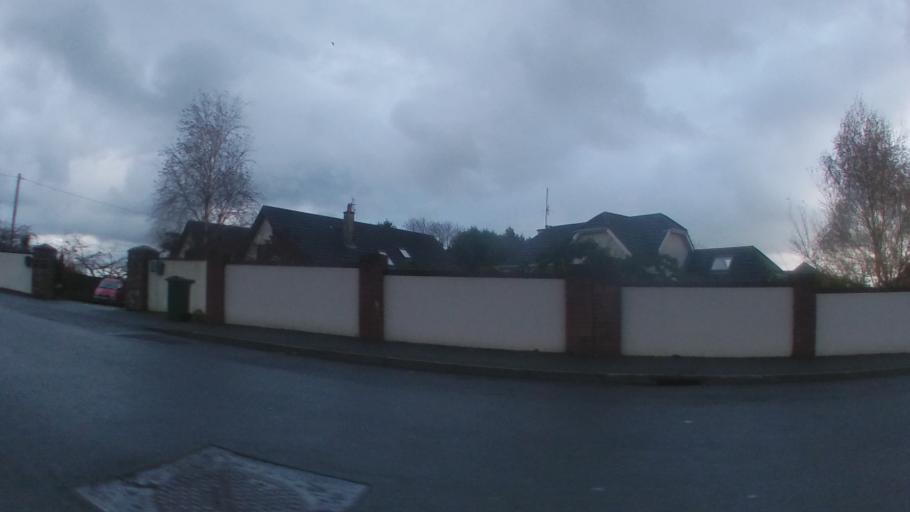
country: IE
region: Leinster
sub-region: Wicklow
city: Kilcoole
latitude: 53.1115
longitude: -6.0606
